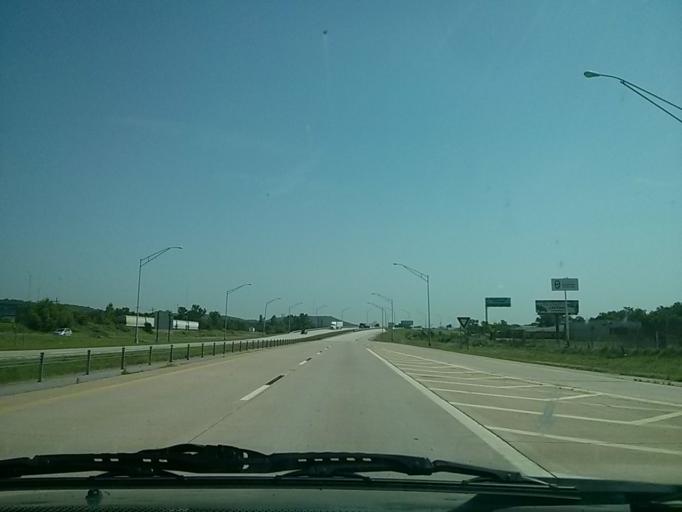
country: US
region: Oklahoma
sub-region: Tulsa County
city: Oakhurst
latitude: 36.0912
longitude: -96.0380
